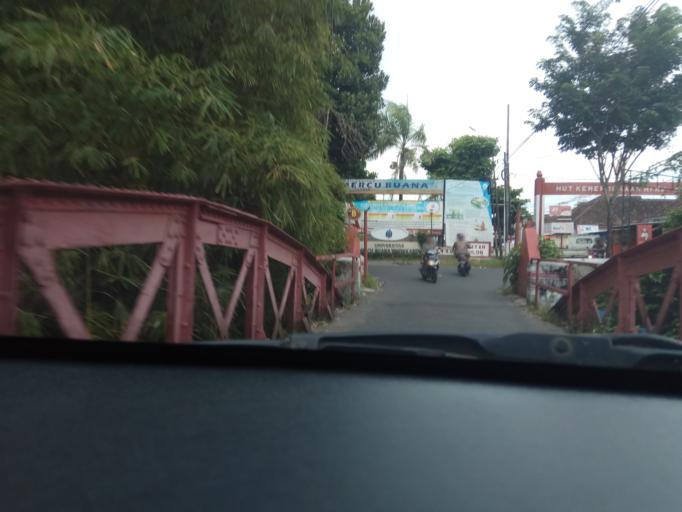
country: ID
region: Daerah Istimewa Yogyakarta
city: Depok
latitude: -7.7634
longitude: 110.3940
